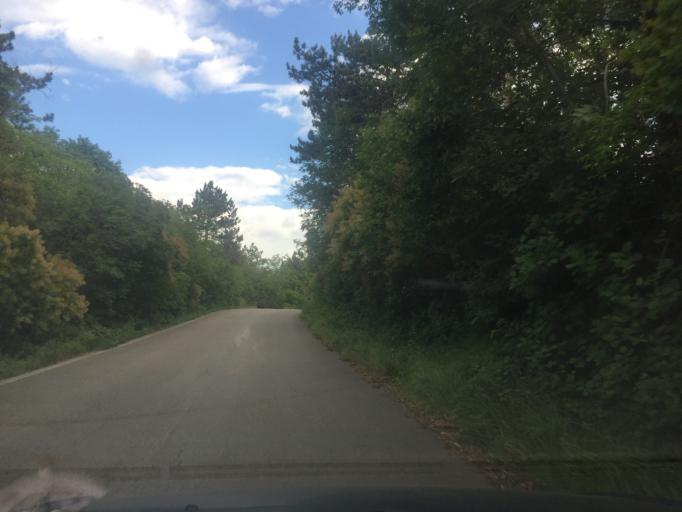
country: IT
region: Friuli Venezia Giulia
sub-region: Provincia di Gorizia
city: Savogna d'Isonzo
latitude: 45.8875
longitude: 13.5657
